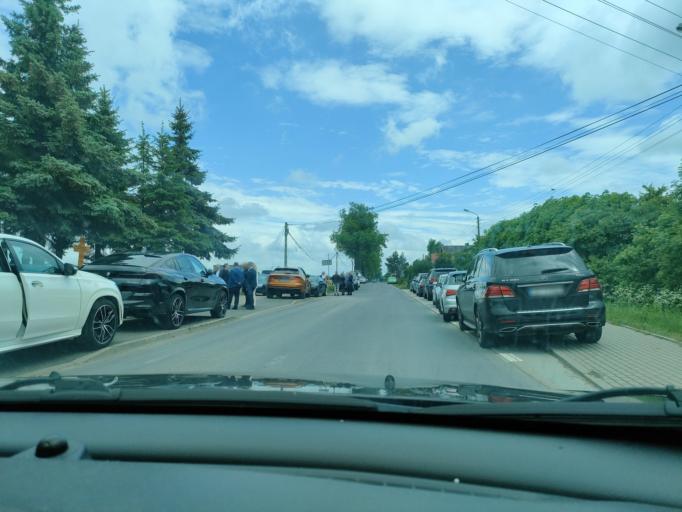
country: PL
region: Kujawsko-Pomorskie
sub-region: Bydgoszcz
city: Fordon
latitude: 53.2119
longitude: 18.1563
